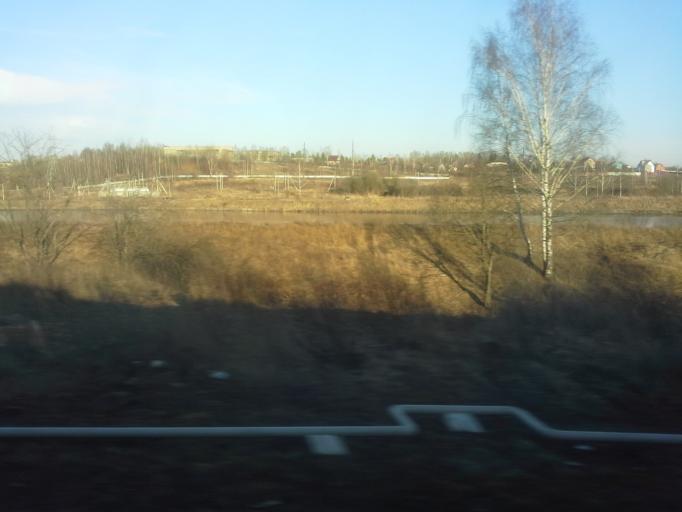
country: RU
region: Moskovskaya
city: Iksha
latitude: 56.1775
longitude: 37.5142
